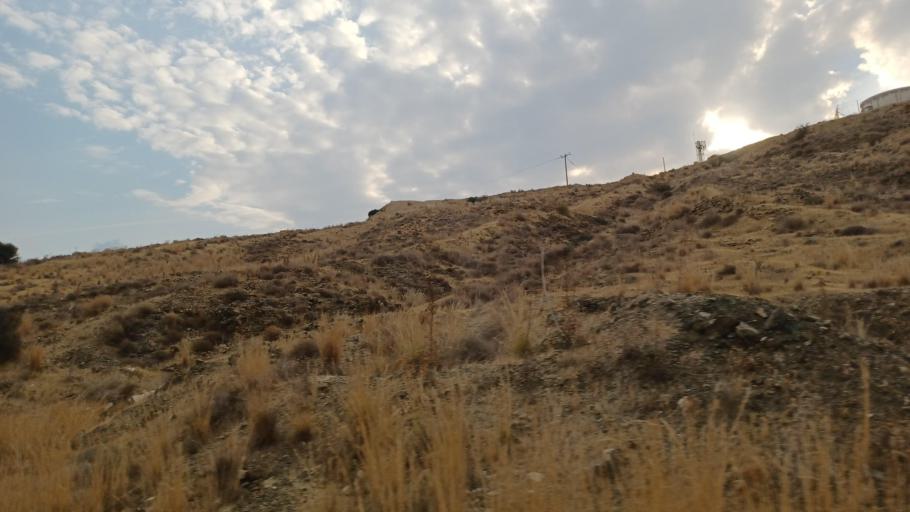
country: CY
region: Larnaka
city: Troulloi
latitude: 35.0158
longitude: 33.5733
